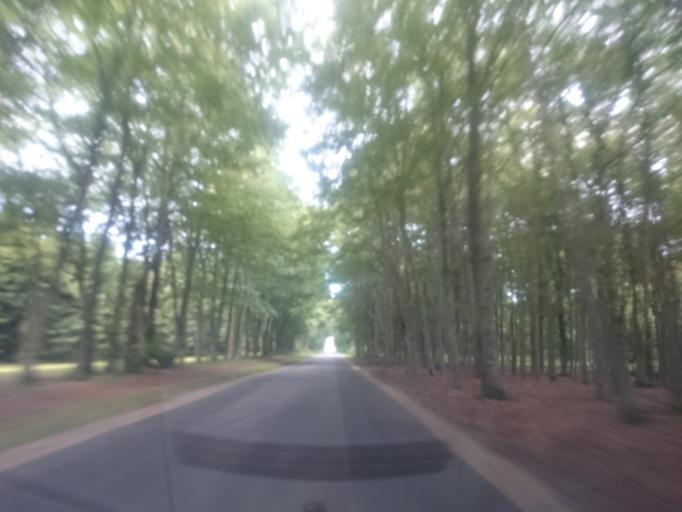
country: DK
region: South Denmark
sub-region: Billund Kommune
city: Grindsted
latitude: 55.6469
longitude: 8.8530
